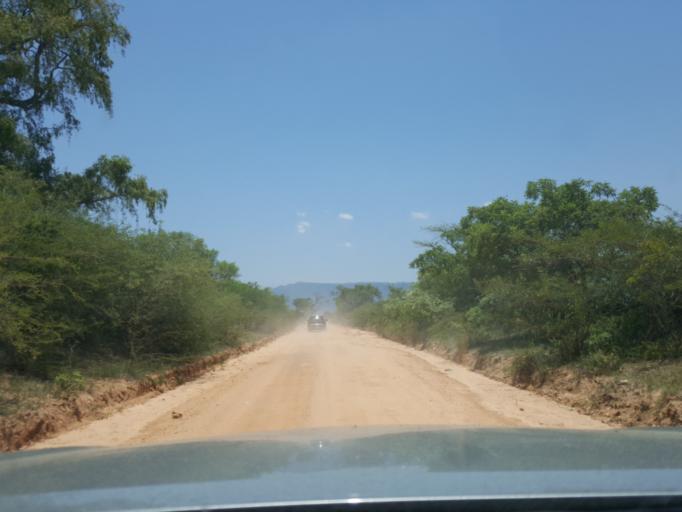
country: ZA
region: Limpopo
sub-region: Mopani District Municipality
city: Hoedspruit
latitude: -24.5793
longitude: 30.9917
